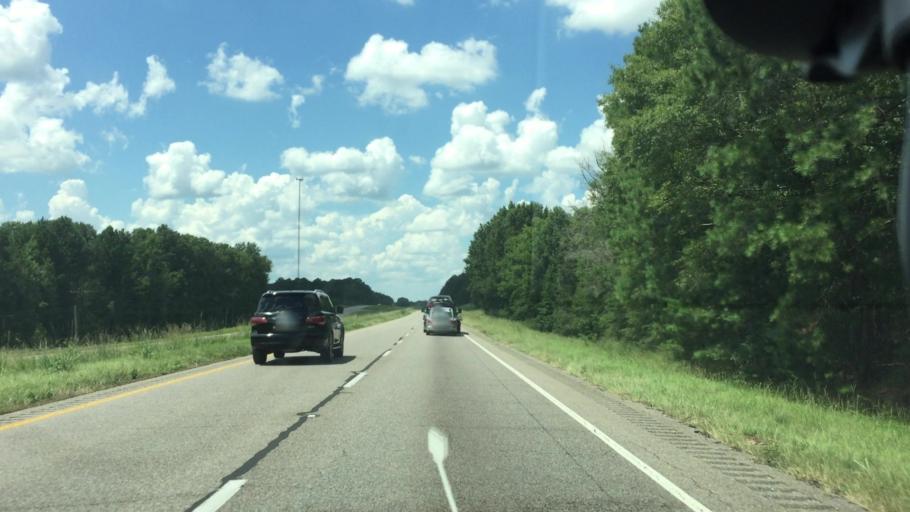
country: US
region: Alabama
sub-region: Montgomery County
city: Pike Road
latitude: 32.1246
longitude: -86.0768
